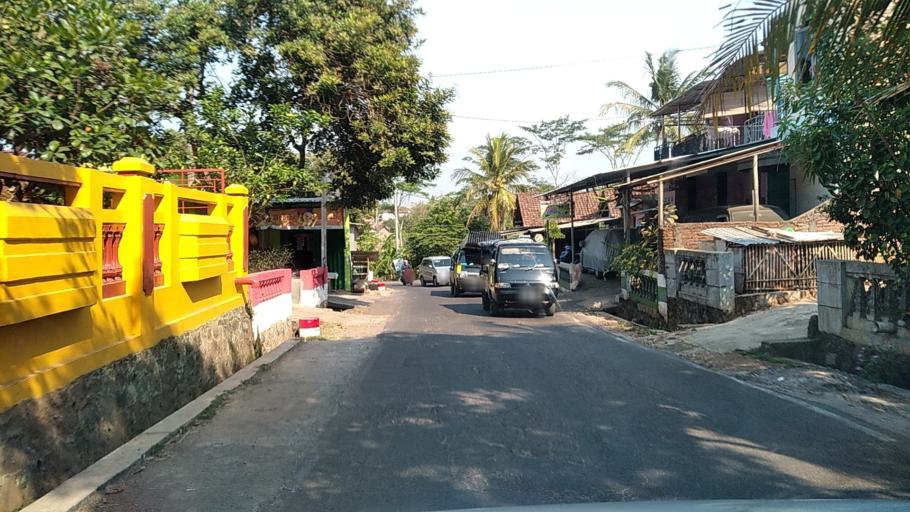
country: ID
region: Central Java
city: Semarang
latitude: -7.0529
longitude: 110.3294
